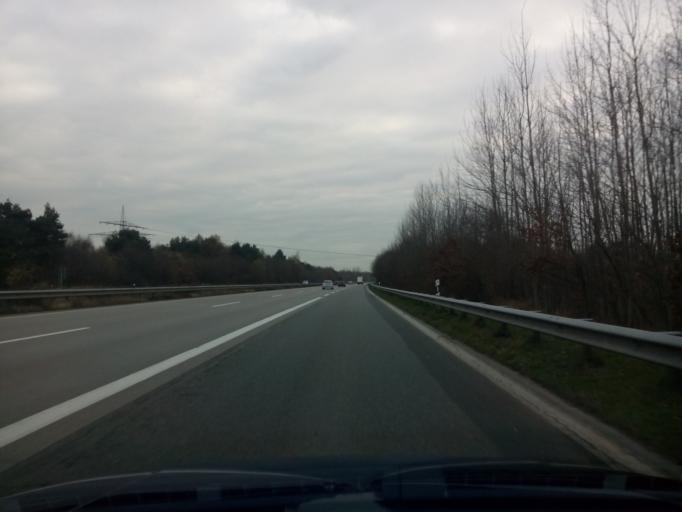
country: DE
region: Lower Saxony
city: Langen
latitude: 53.6071
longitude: 8.6574
